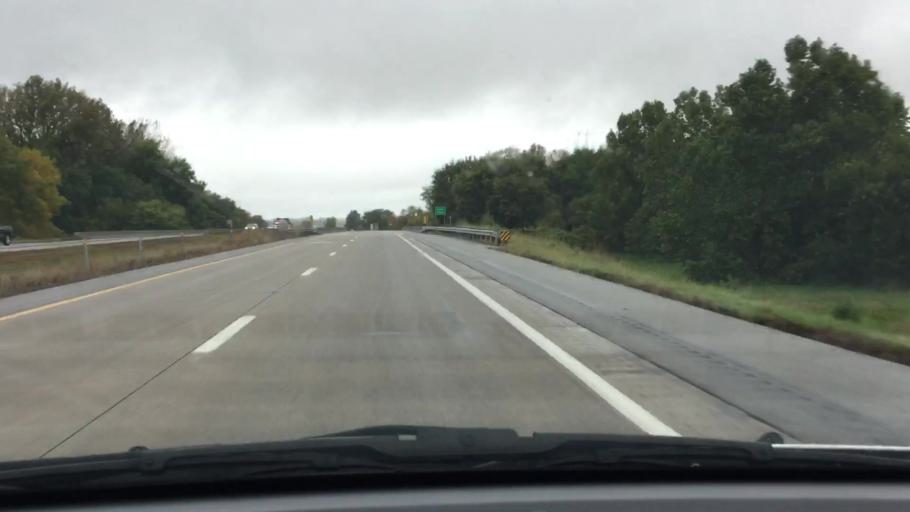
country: US
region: Iowa
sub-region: Jasper County
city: Colfax
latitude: 41.6972
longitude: -93.1965
